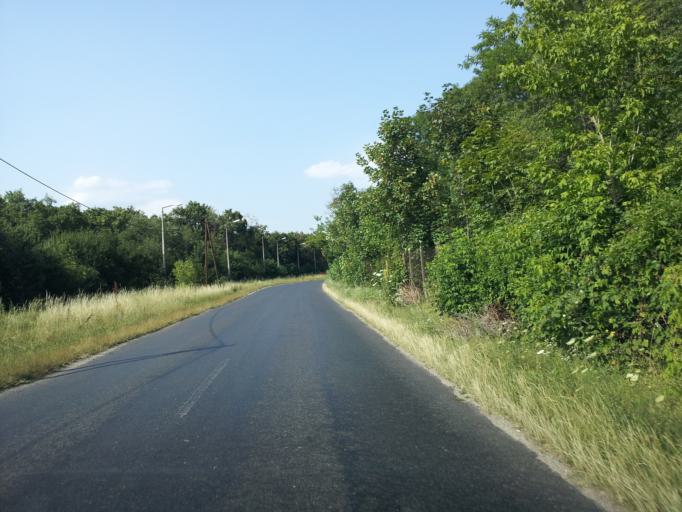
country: HU
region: Veszprem
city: Berhida
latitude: 47.1068
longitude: 18.0983
